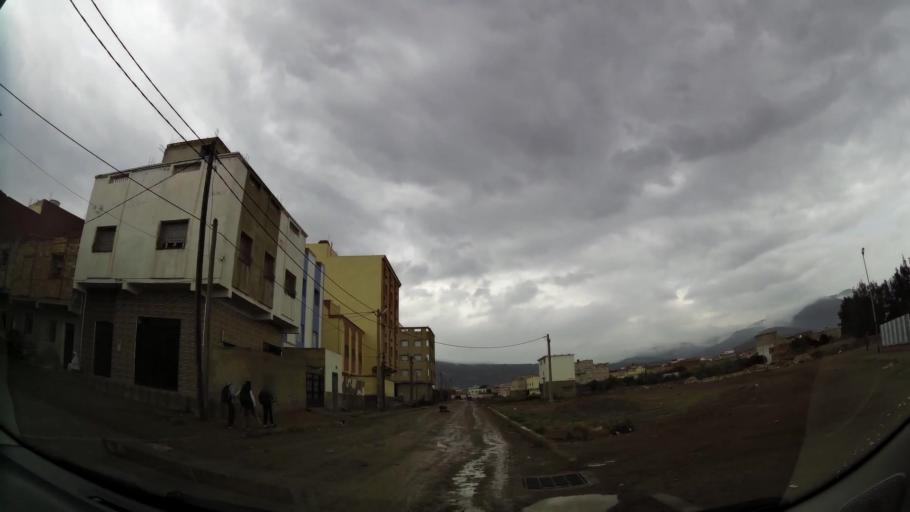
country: MA
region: Oriental
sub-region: Nador
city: Nador
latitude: 35.1474
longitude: -2.9798
